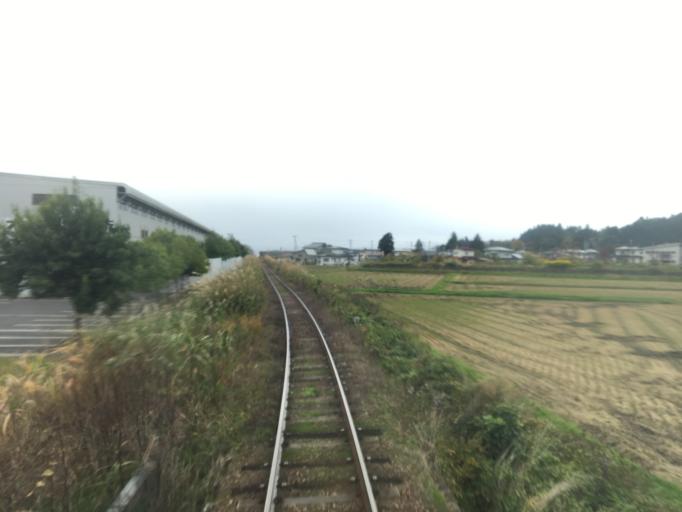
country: JP
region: Yamagata
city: Takahata
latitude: 38.0714
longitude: 140.1293
